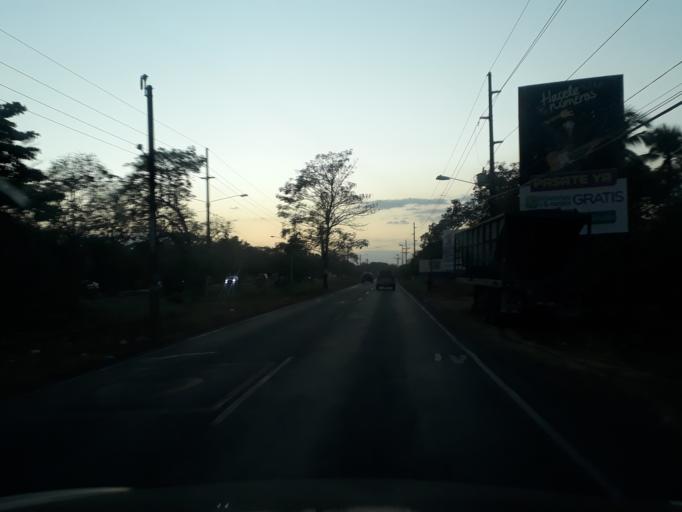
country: CR
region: Puntarenas
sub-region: Canton Central de Puntarenas
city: Chacarita
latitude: 9.9783
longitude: -84.7587
